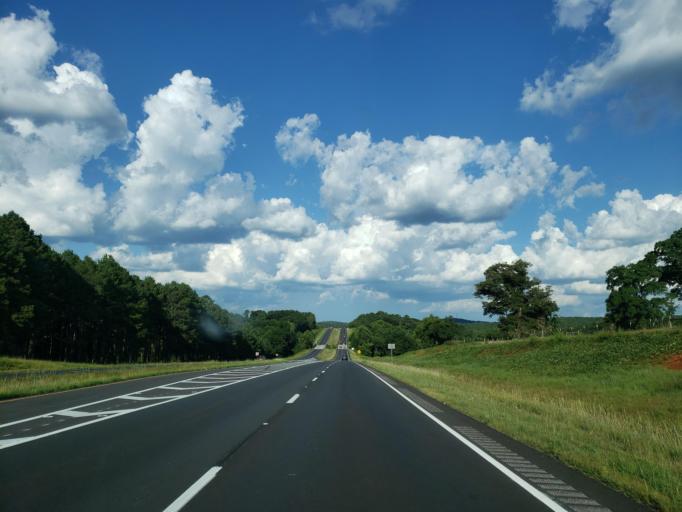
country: US
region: Georgia
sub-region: Floyd County
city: Lindale
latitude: 34.2062
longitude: -85.0803
